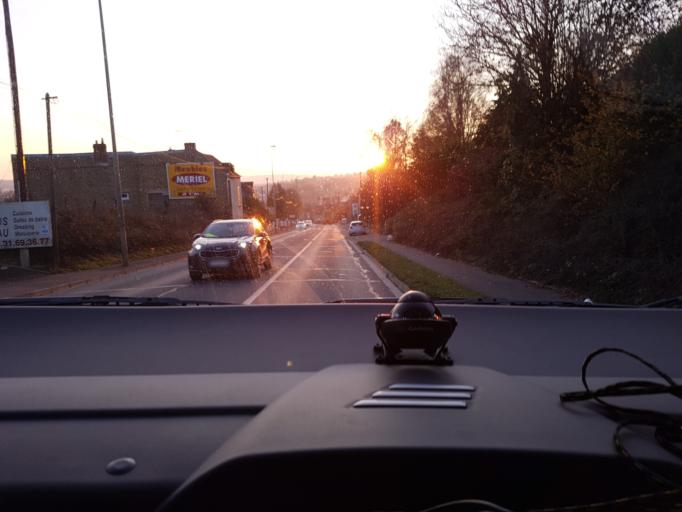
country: FR
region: Lower Normandy
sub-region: Departement du Calvados
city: Conde-sur-Noireau
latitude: 48.8548
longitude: -0.5430
